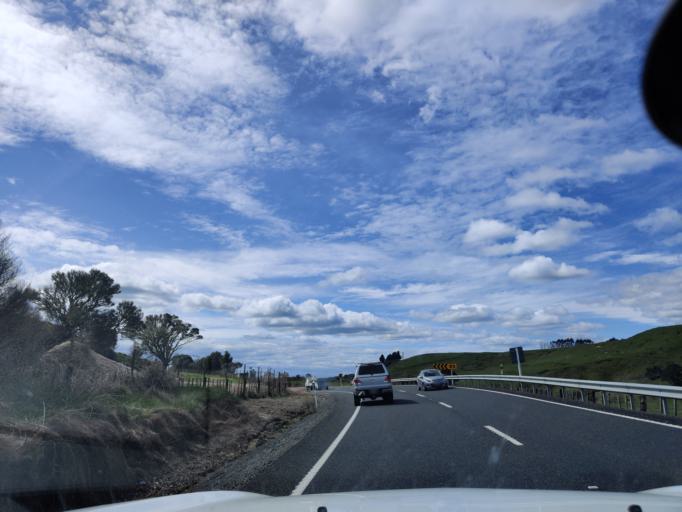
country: NZ
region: Waikato
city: Turangi
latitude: -39.0807
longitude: 175.3808
